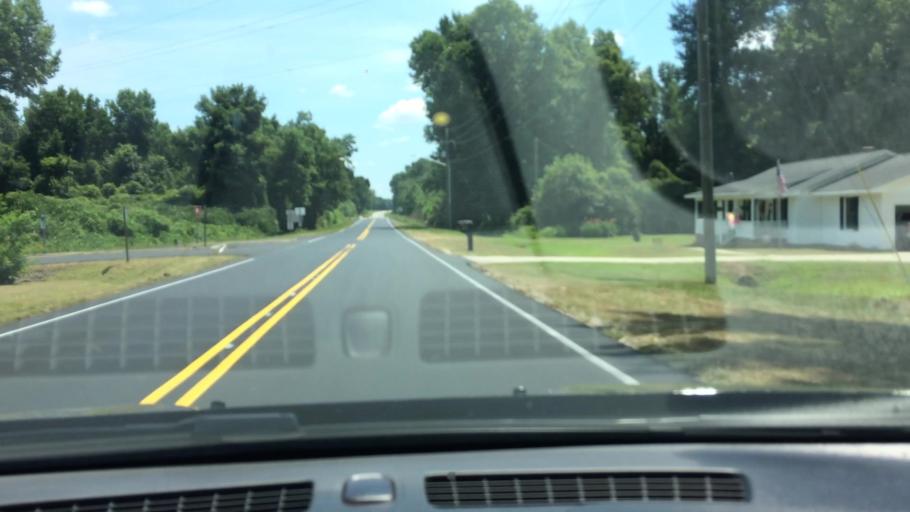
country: US
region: North Carolina
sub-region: Pitt County
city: Ayden
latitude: 35.4709
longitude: -77.4035
